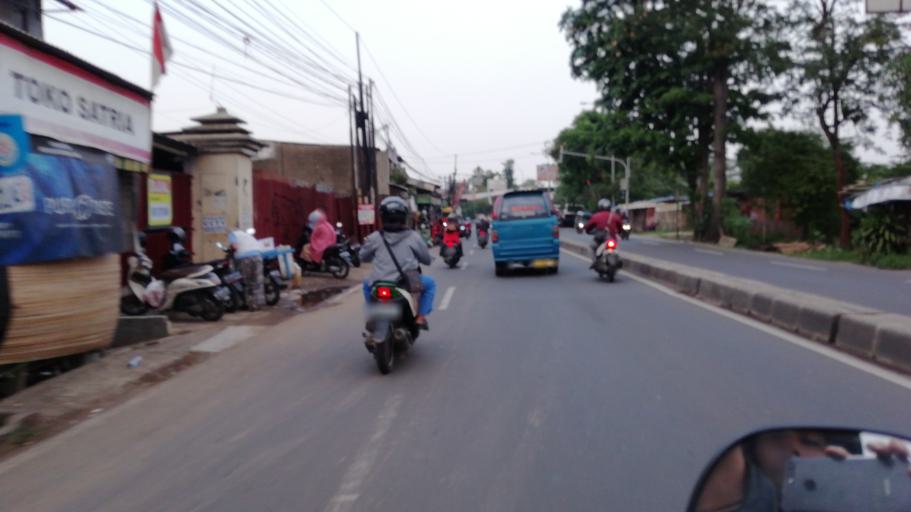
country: ID
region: West Java
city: Cibinong
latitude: -6.4351
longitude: 106.8538
